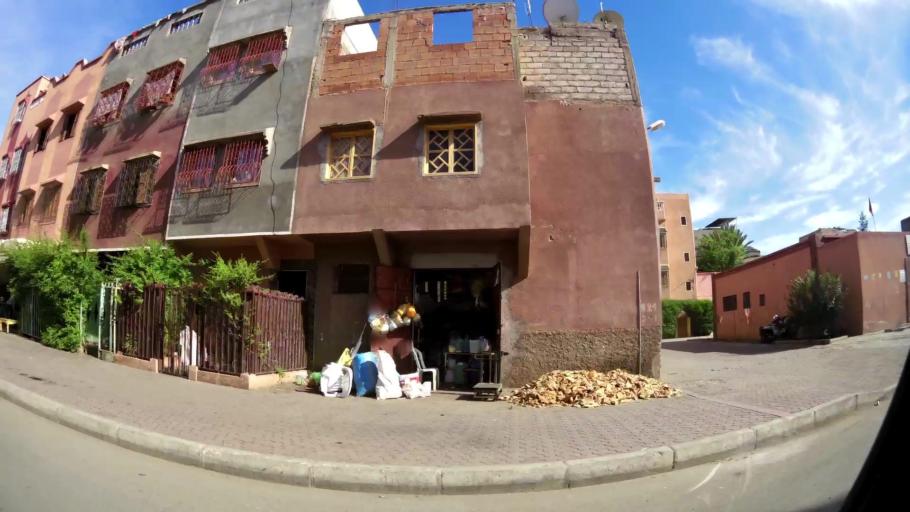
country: MA
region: Marrakech-Tensift-Al Haouz
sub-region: Marrakech
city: Marrakesh
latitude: 31.6067
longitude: -7.9606
